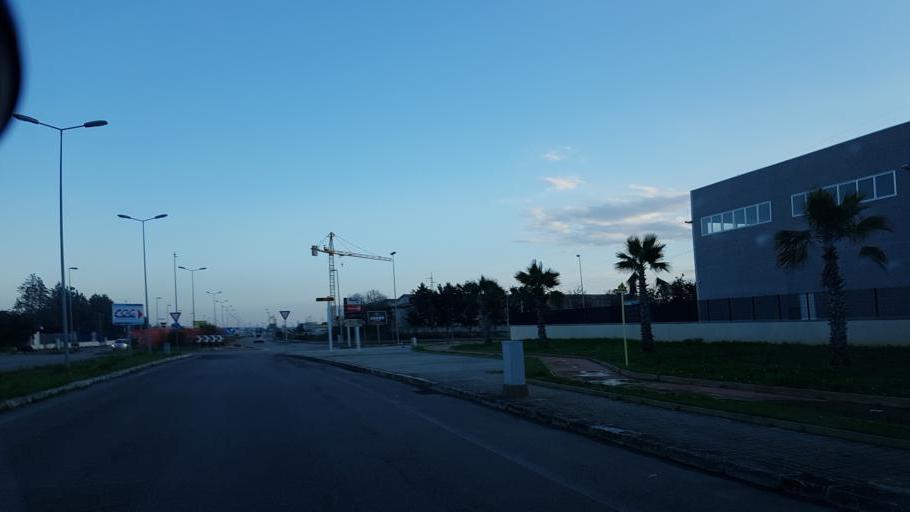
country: IT
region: Apulia
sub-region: Provincia di Lecce
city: Surbo
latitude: 40.3777
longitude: 18.1295
